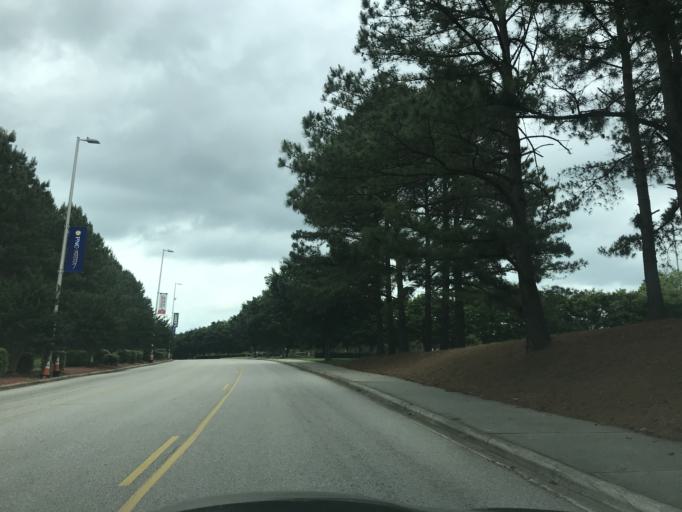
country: US
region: North Carolina
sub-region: Wake County
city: Cary
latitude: 35.8005
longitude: -78.7246
